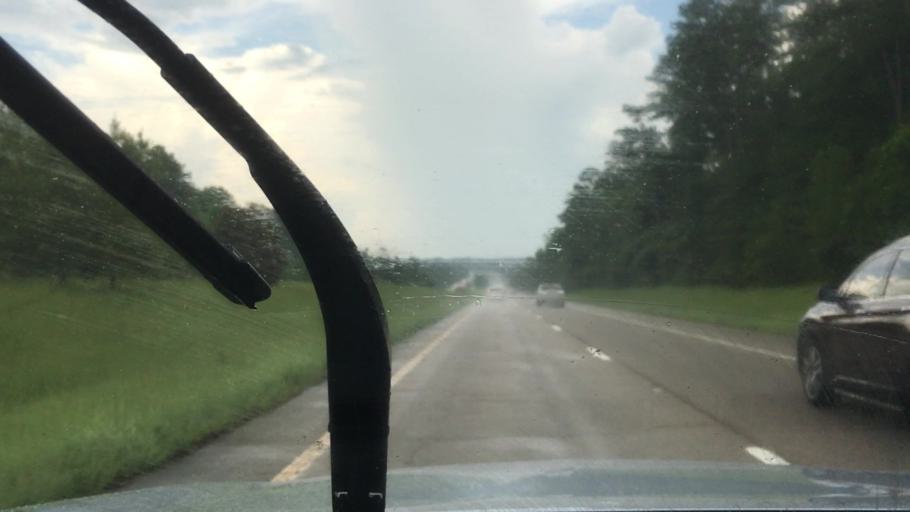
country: US
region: Mississippi
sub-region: Lamar County
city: Purvis
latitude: 31.1599
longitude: -89.3570
